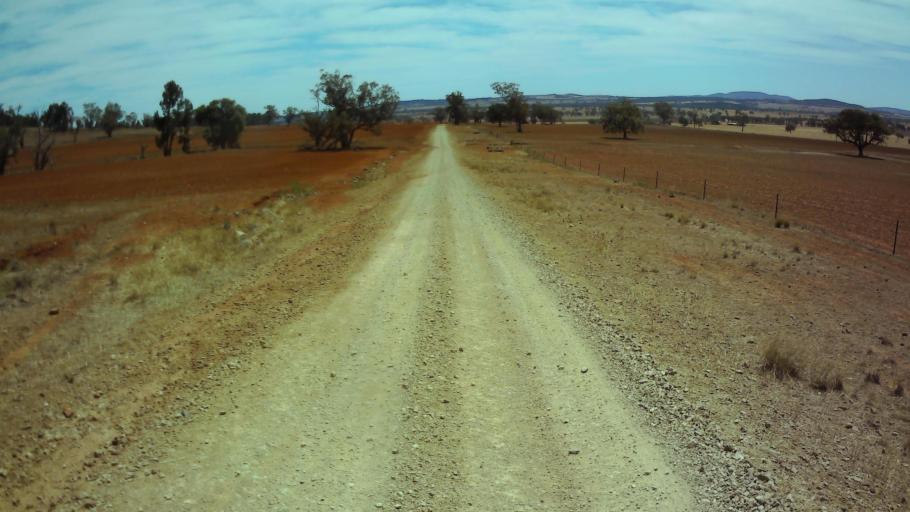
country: AU
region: New South Wales
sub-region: Weddin
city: Grenfell
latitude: -33.7484
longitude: 148.1651
